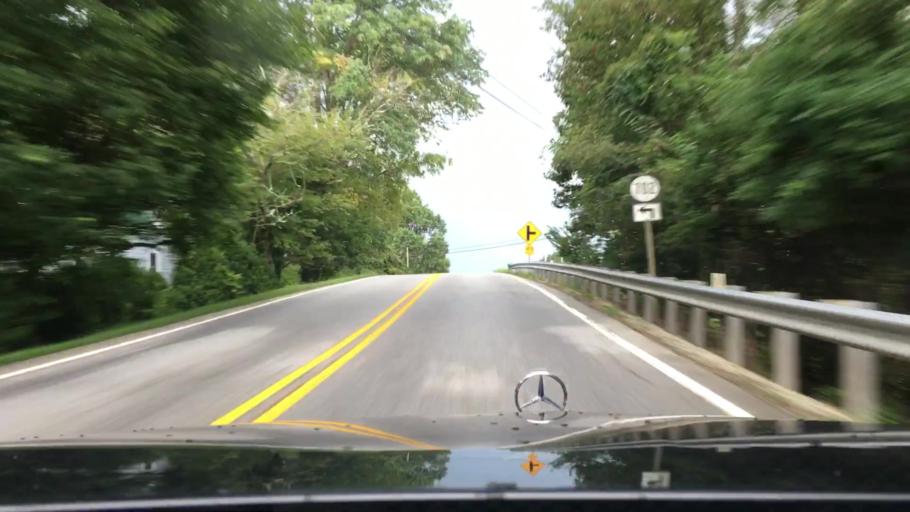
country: US
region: Virginia
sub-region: Nelson County
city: Lovingston
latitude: 37.7854
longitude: -78.9779
